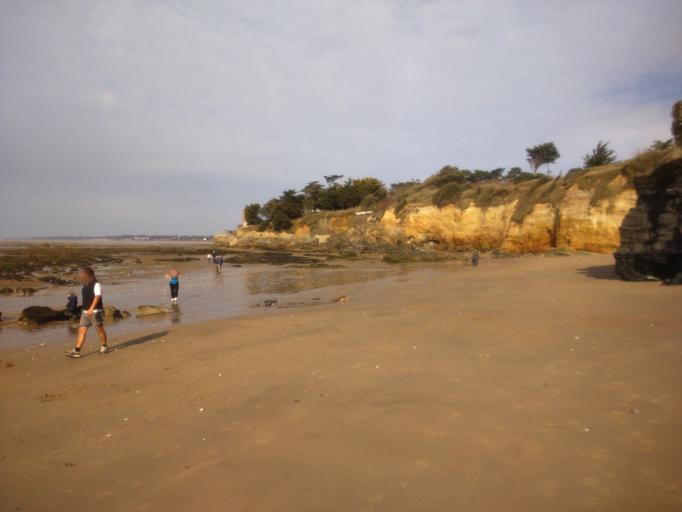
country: FR
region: Pays de la Loire
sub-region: Departement de la Loire-Atlantique
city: La Bernerie-en-Retz
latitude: 47.0848
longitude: -2.0459
